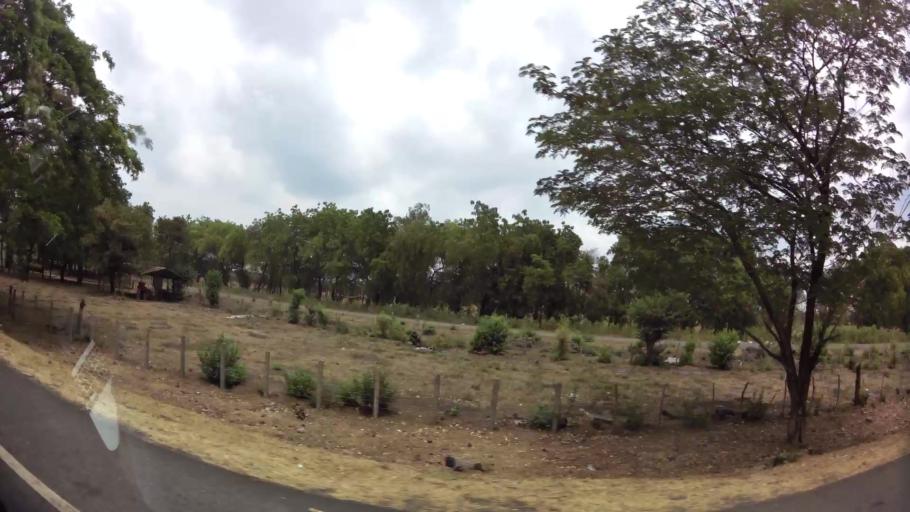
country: NI
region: Leon
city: Telica
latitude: 12.5107
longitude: -86.8604
